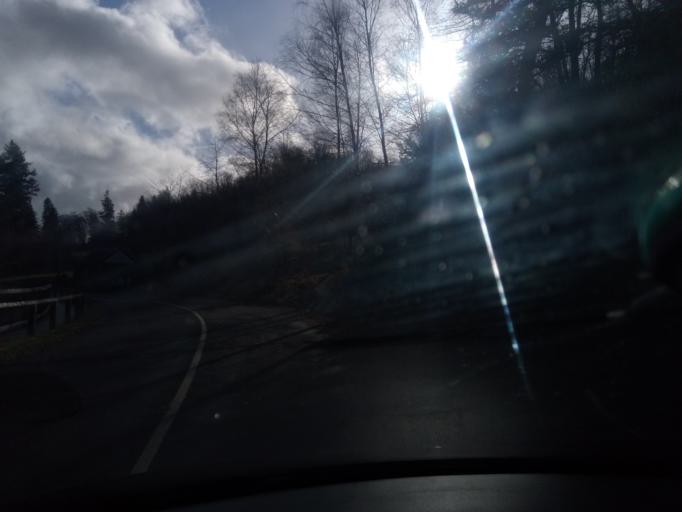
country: GB
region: England
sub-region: Northumberland
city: Rothbury
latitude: 55.3167
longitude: -1.8925
